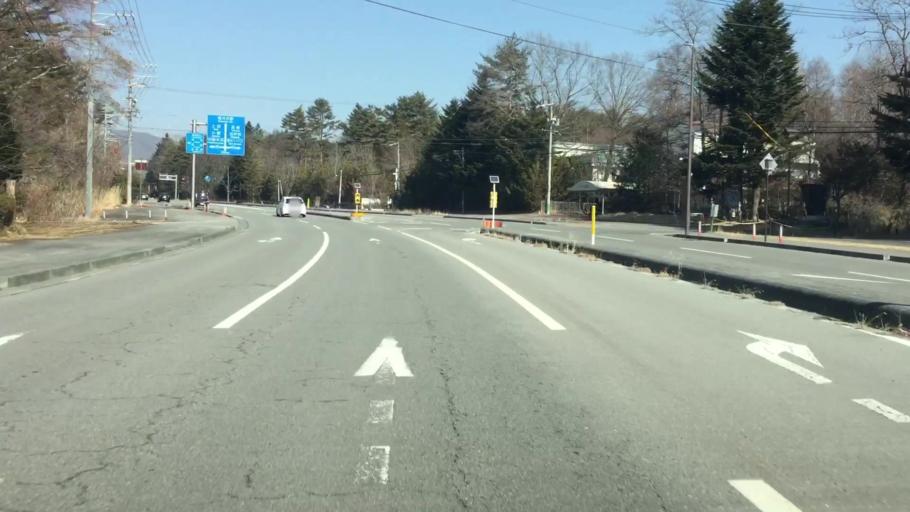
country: JP
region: Nagano
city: Saku
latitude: 36.3194
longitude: 138.6308
